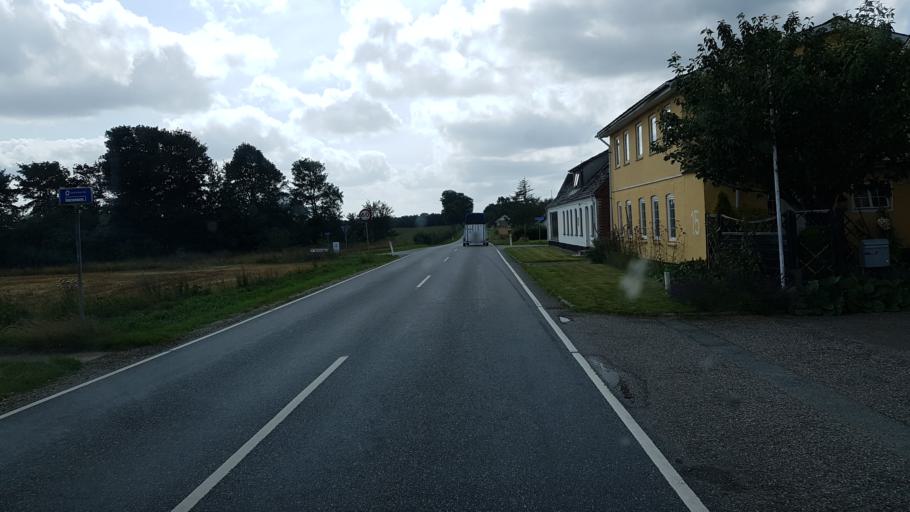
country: DK
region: South Denmark
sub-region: Vejen Kommune
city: Brorup
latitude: 55.5347
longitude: 9.0550
